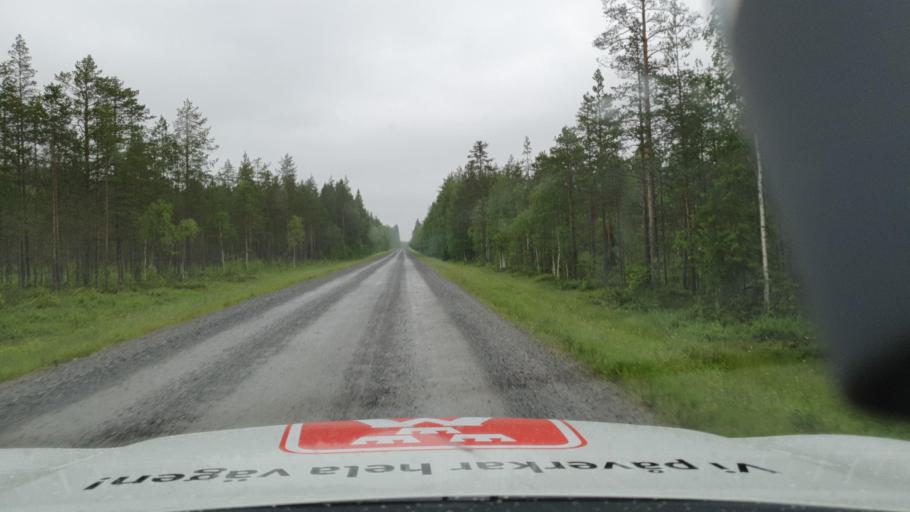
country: SE
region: Vaesterbotten
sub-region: Nordmalings Kommun
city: Nordmaling
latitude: 63.8243
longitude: 19.4918
